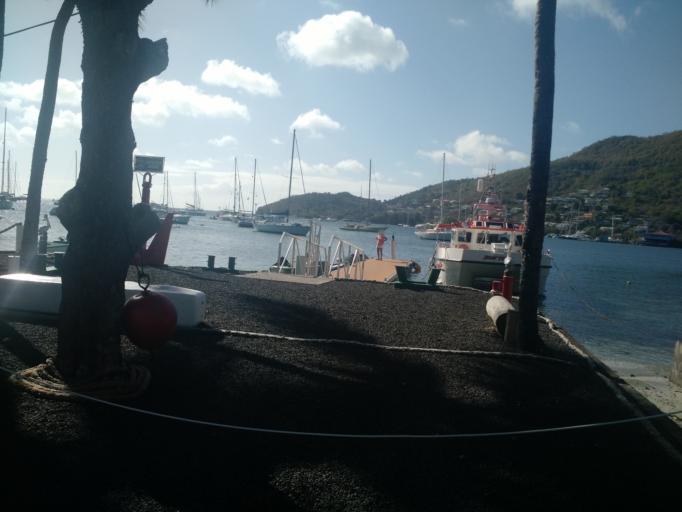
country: VC
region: Grenadines
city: Port Elizabeth
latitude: 13.0092
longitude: -61.2359
